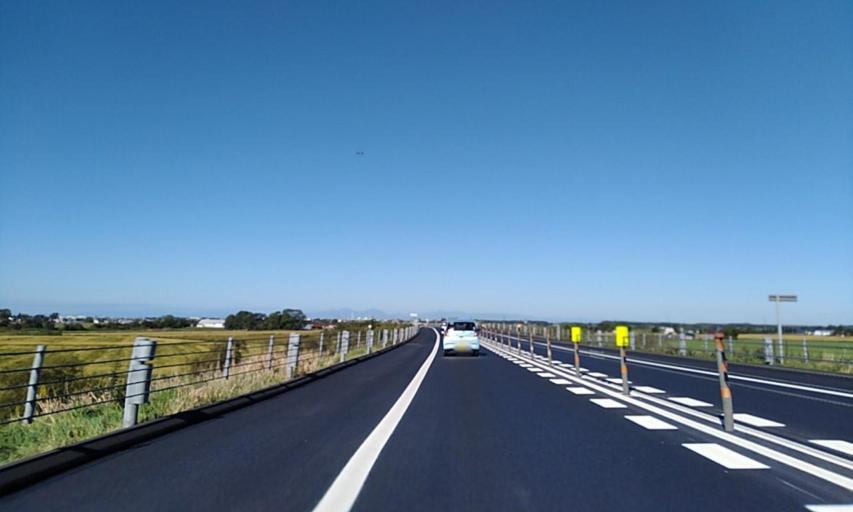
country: JP
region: Hokkaido
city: Tomakomai
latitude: 42.5767
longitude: 141.9652
